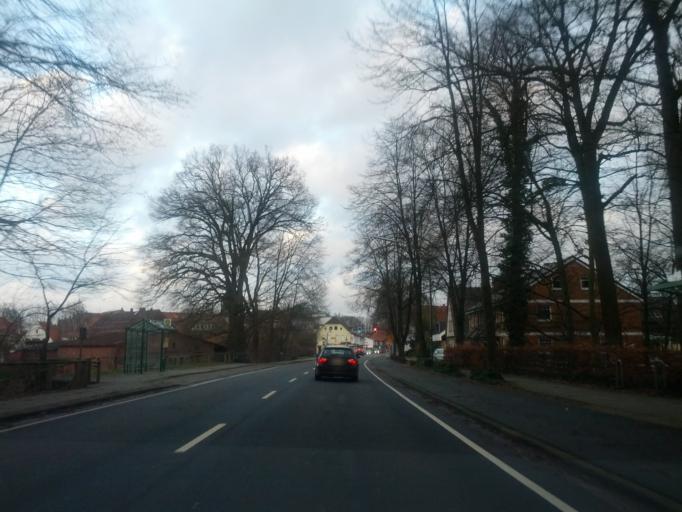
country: DE
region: Lower Saxony
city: Scheessel
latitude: 53.1666
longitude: 9.4796
